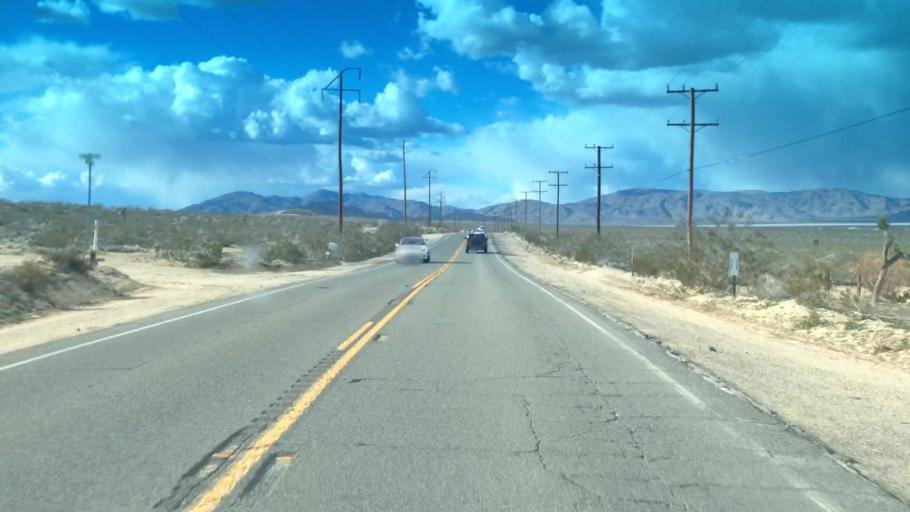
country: US
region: California
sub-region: San Bernardino County
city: Lucerne Valley
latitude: 34.4169
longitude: -116.9106
